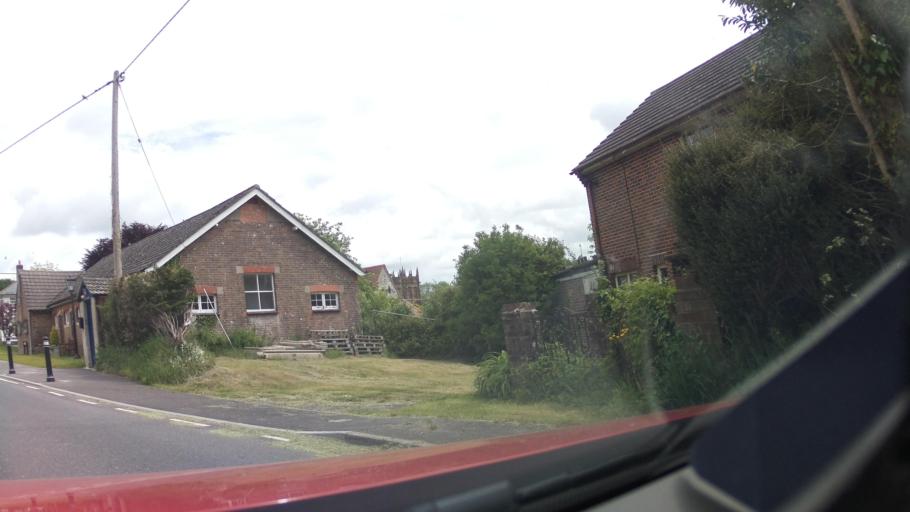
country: GB
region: England
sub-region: Dorset
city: Dorchester
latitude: 50.7321
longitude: -2.4584
